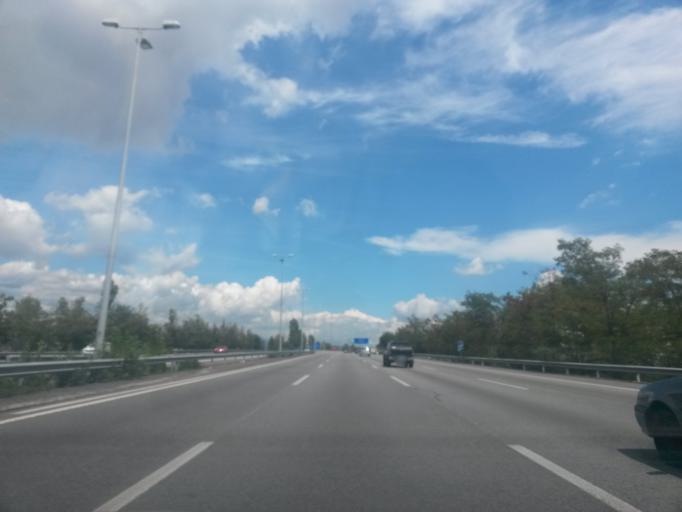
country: ES
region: Catalonia
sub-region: Provincia de Barcelona
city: Montornes del Valles
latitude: 41.5630
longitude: 2.2719
